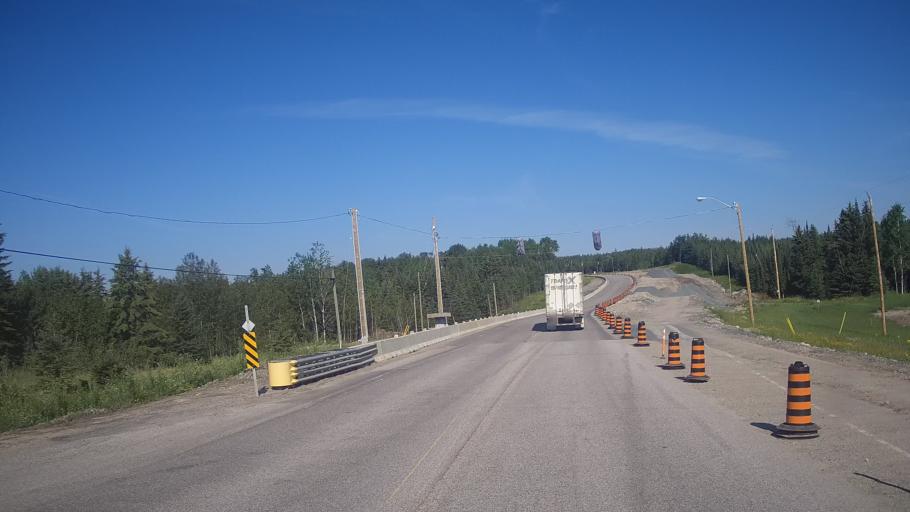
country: CA
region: Ontario
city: Dryden
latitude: 49.6908
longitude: -92.5260
